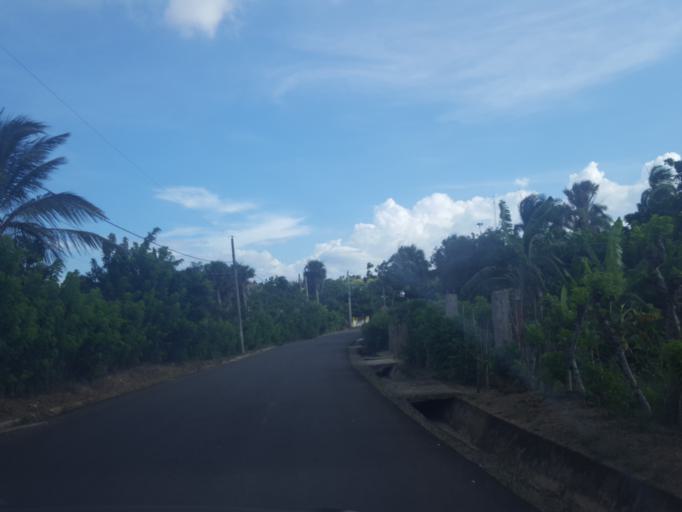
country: DO
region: Santiago
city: Licey al Medio
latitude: 19.3616
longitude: -70.6327
